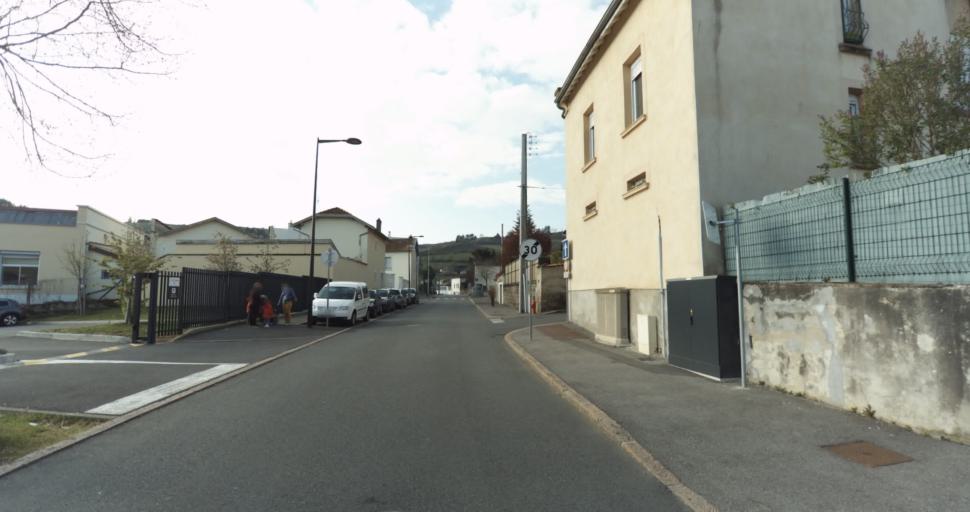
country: FR
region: Rhone-Alpes
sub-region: Departement du Rhone
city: Tarare
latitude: 45.8887
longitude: 4.4378
